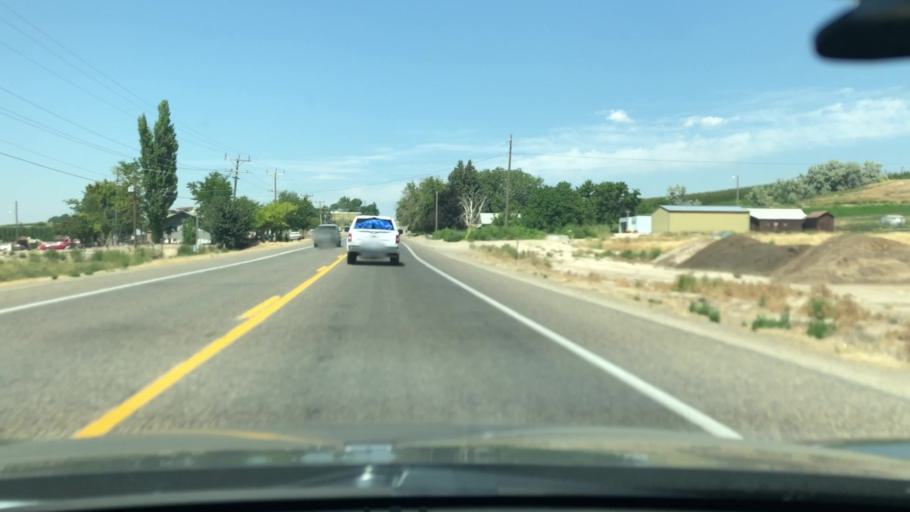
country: US
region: Idaho
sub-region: Canyon County
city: Wilder
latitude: 43.6532
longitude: -116.9120
